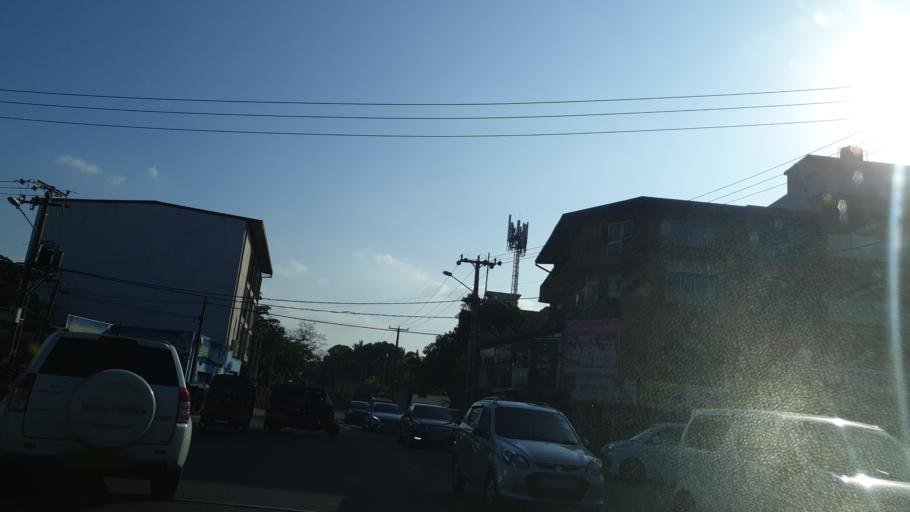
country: LK
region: Western
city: Sri Jayewardenepura Kotte
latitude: 6.8697
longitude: 79.8980
